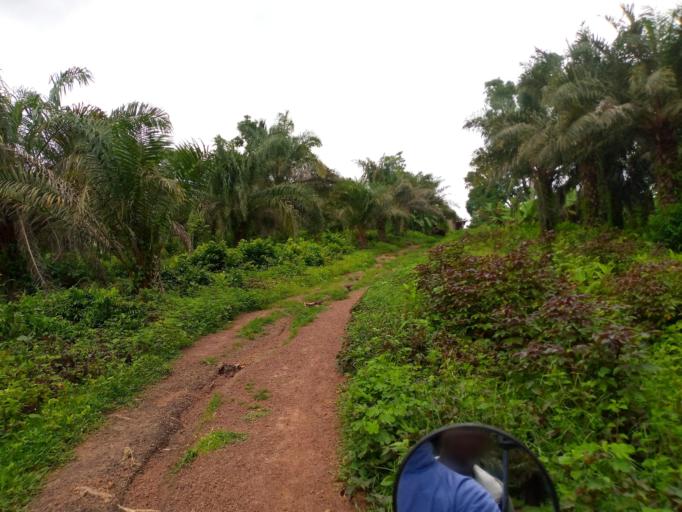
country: SL
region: Northern Province
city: Mange
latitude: 8.9875
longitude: -12.7194
